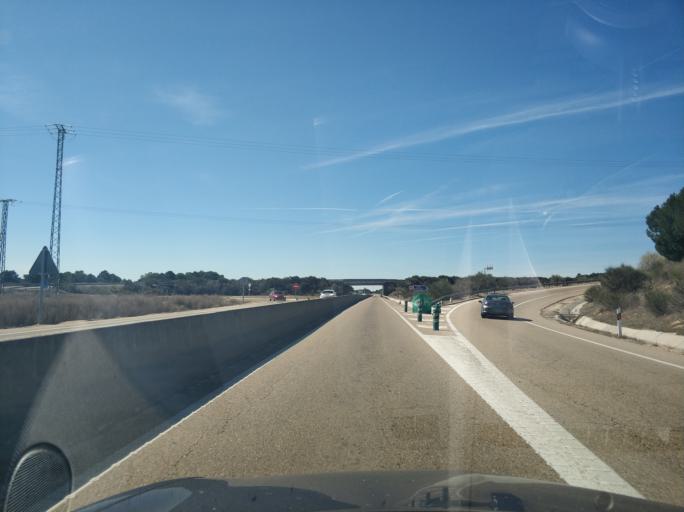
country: ES
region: Castille and Leon
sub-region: Provincia de Valladolid
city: Boecillo
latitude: 41.5370
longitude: -4.7012
